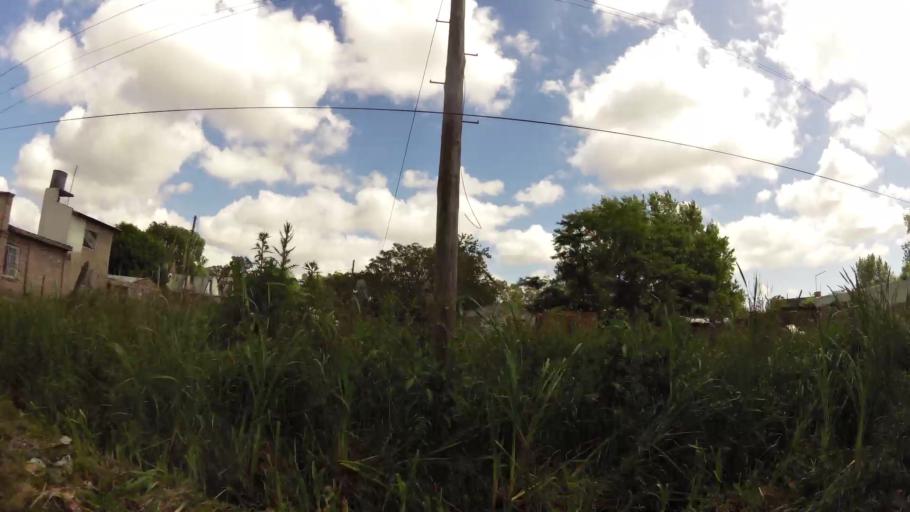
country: AR
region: Buenos Aires
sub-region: Partido de Quilmes
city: Quilmes
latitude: -34.8359
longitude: -58.2230
